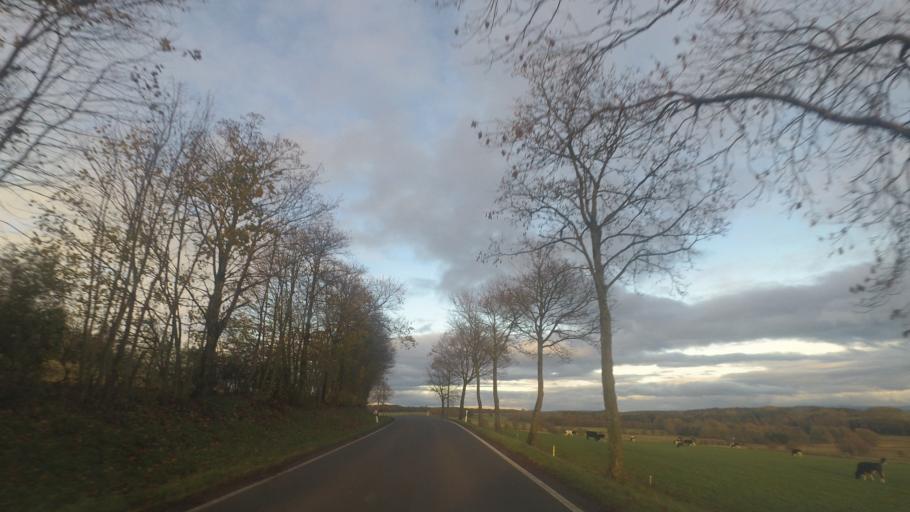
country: DE
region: Hesse
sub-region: Regierungsbezirk Giessen
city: Freiensteinau
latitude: 50.4642
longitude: 9.4058
